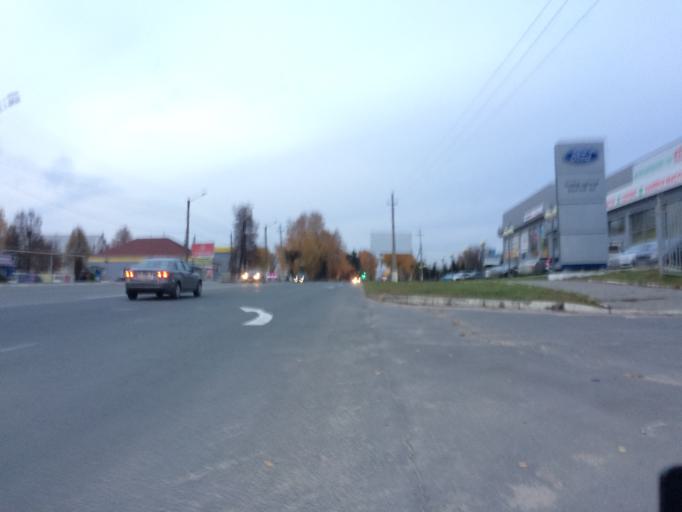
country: RU
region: Mariy-El
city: Yoshkar-Ola
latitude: 56.6063
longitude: 47.8806
